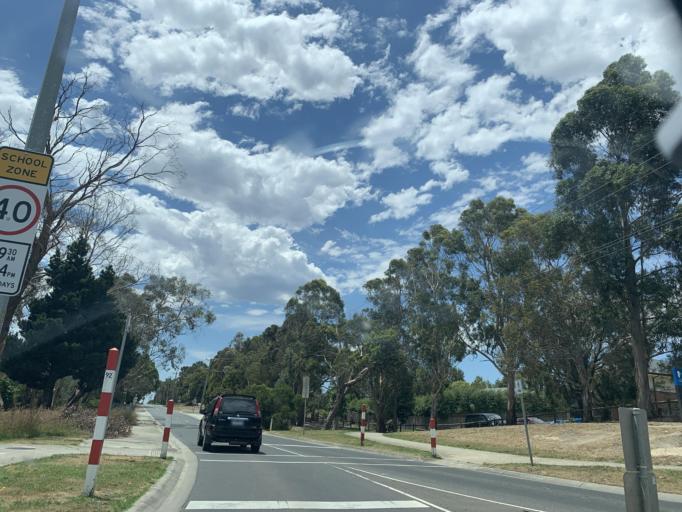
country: AU
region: Victoria
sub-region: Casey
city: Cranbourne South
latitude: -38.1477
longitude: 145.2455
